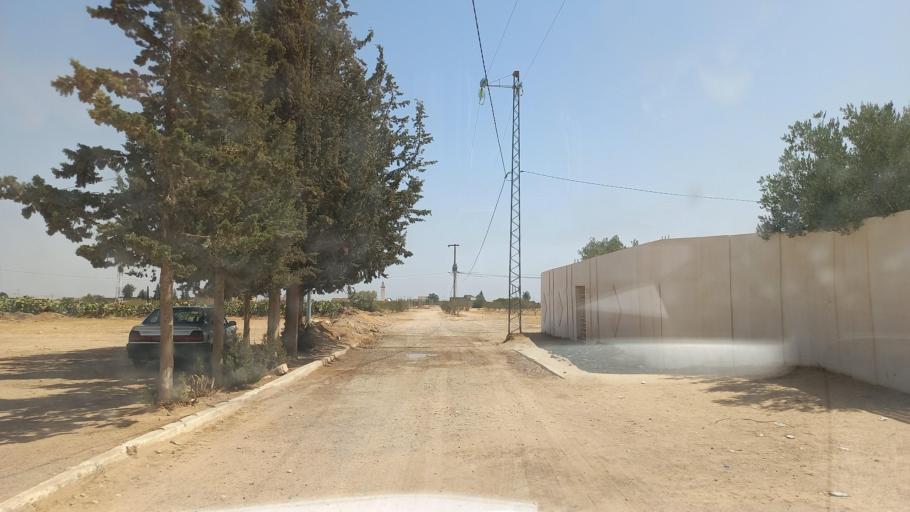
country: TN
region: Al Qasrayn
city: Kasserine
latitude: 35.2541
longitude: 9.0202
